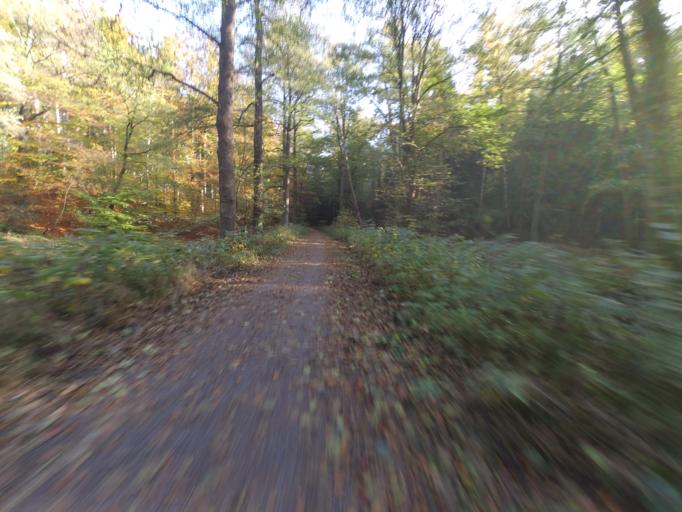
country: DE
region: Saxony
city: Radeberg
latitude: 51.0943
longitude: 13.8497
